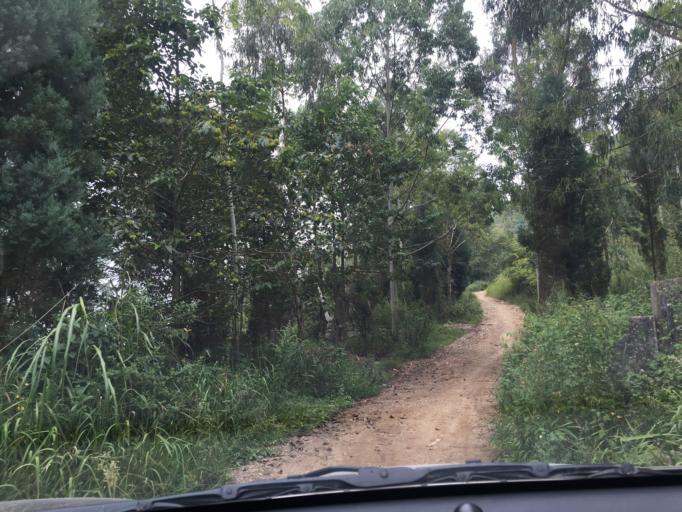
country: CN
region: Guangxi Zhuangzu Zizhiqu
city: Xinzhou
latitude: 25.3775
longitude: 105.6321
